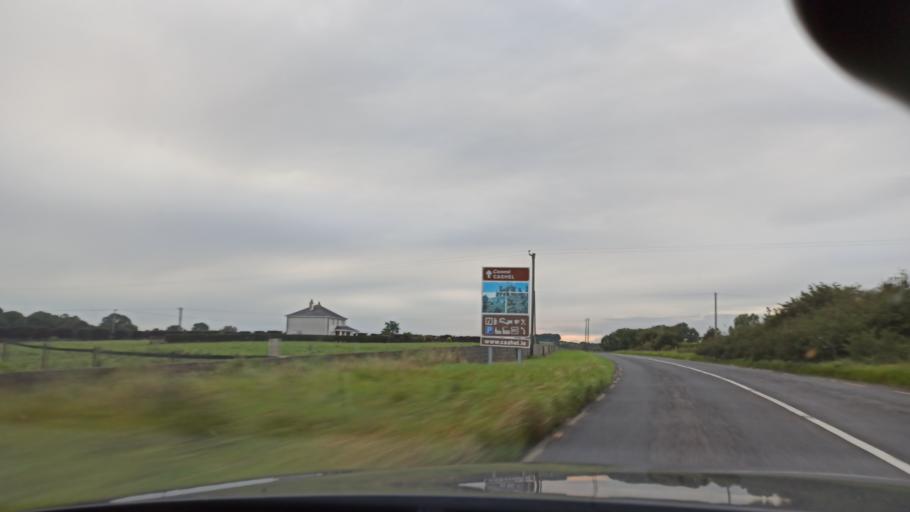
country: IE
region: Munster
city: Cashel
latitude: 52.5006
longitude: -7.8702
